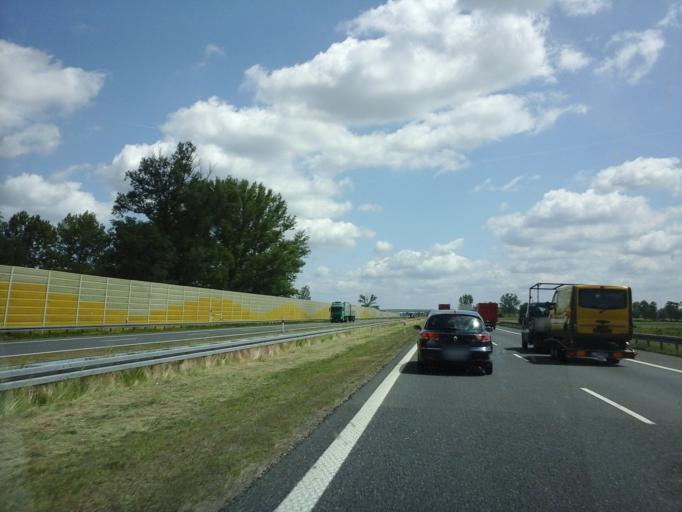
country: PL
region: Lodz Voivodeship
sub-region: Powiat poddebicki
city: Wartkowice
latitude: 52.0077
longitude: 18.9782
